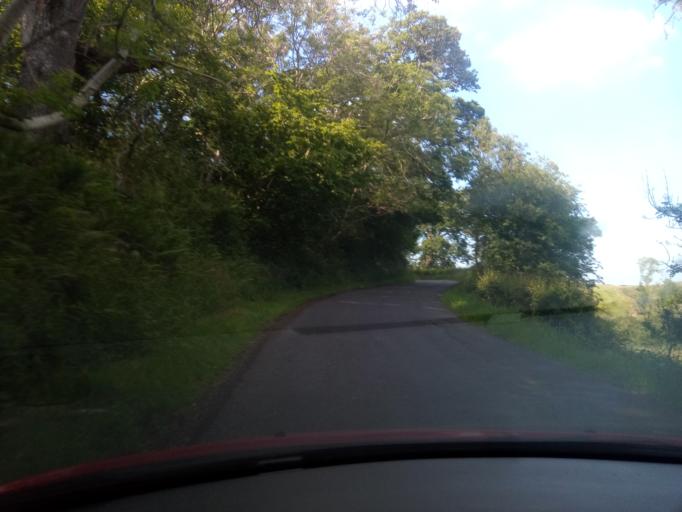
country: GB
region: Scotland
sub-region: The Scottish Borders
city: Innerleithen
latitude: 55.5004
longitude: -2.9833
